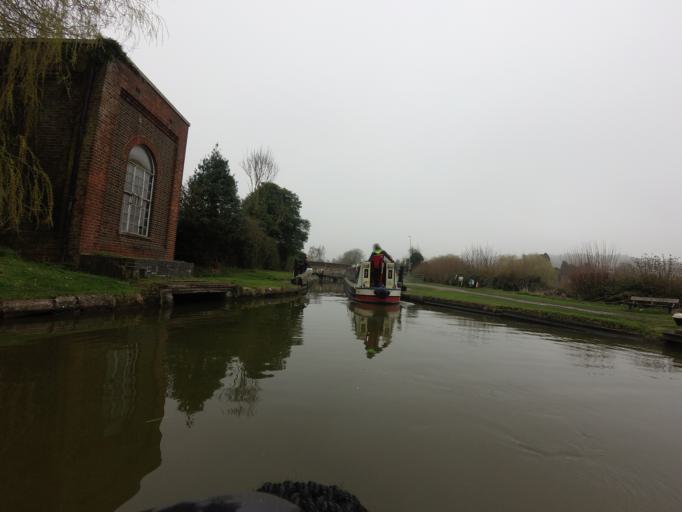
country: GB
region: England
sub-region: Hertfordshire
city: Berkhamsted
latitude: 51.7715
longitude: -0.5888
